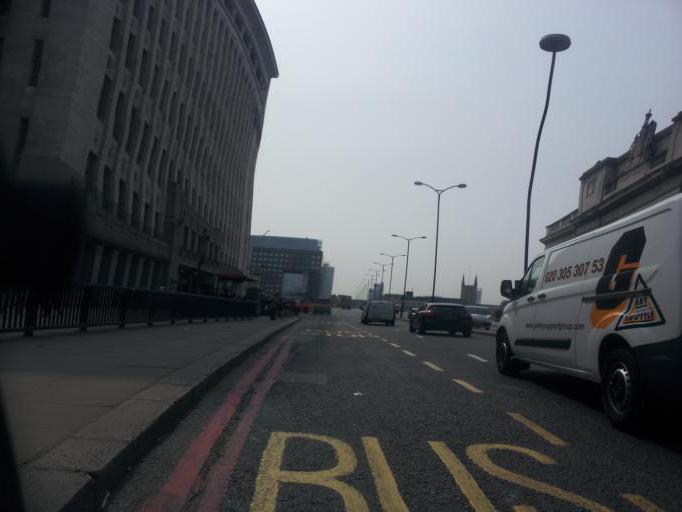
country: GB
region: England
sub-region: Greater London
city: City of London
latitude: 51.5098
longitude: -0.0873
